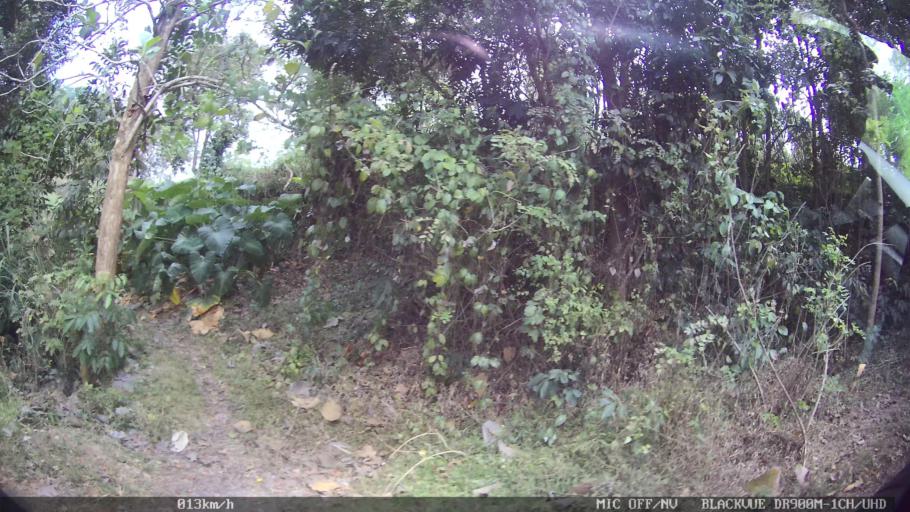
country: ID
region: Central Java
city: Candi Prambanan
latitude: -7.8171
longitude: 110.5251
